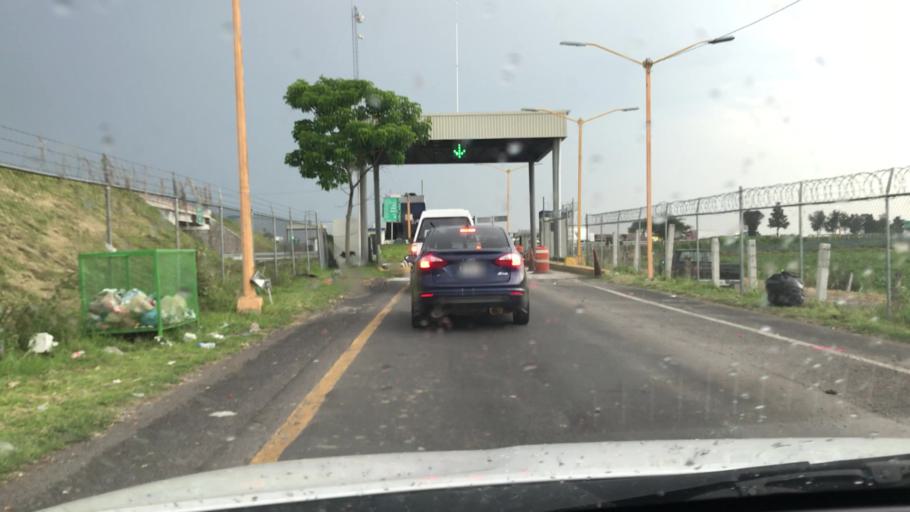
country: MX
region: Michoacan
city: Vistahermosa de Negrete
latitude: 20.2698
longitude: -102.4395
